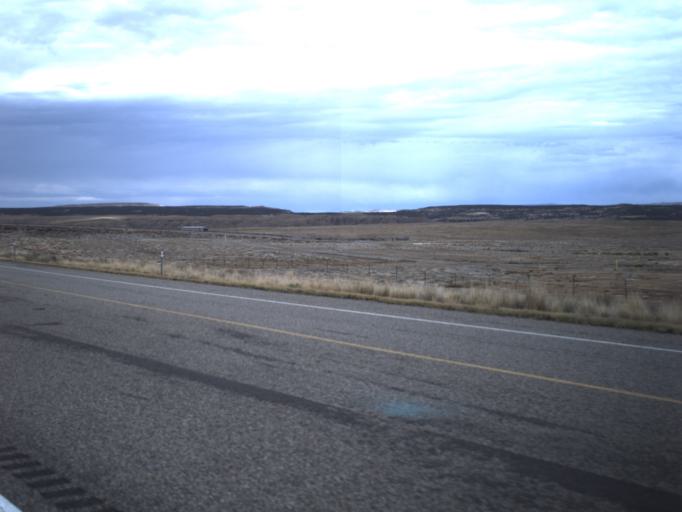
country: US
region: Colorado
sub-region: Mesa County
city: Loma
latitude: 39.1108
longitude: -109.1876
